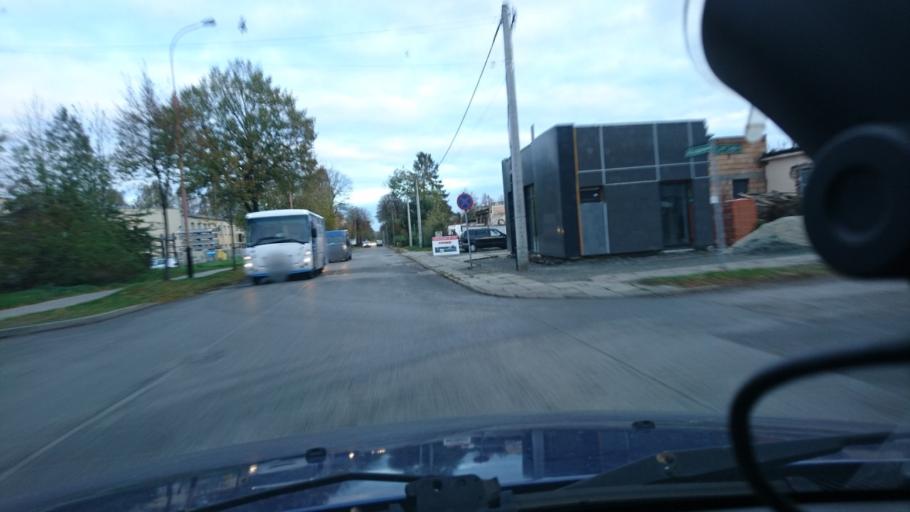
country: PL
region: Silesian Voivodeship
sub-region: Bielsko-Biala
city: Bielsko-Biala
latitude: 49.8286
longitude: 19.0552
